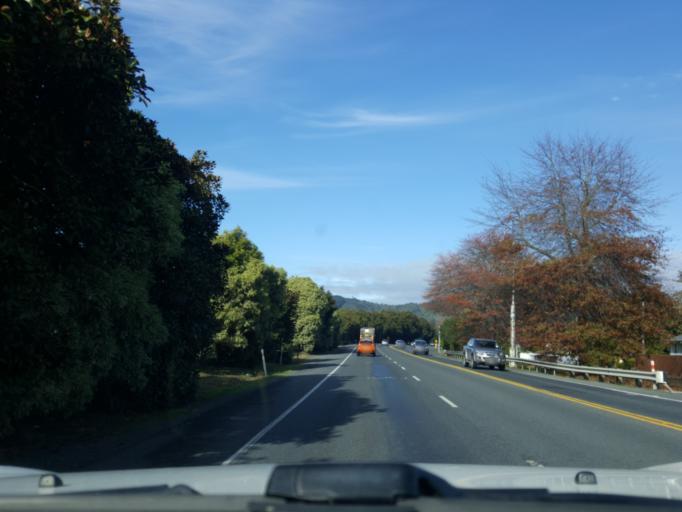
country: NZ
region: Waikato
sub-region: Waikato District
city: Ngaruawahia
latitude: -37.5816
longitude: 175.1592
